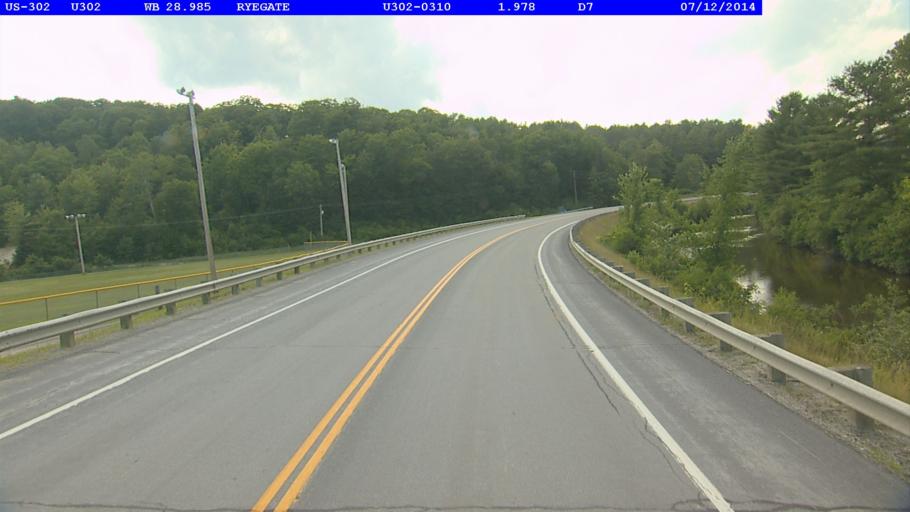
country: US
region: New Hampshire
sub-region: Grafton County
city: Woodsville
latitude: 44.1873
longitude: -72.1427
